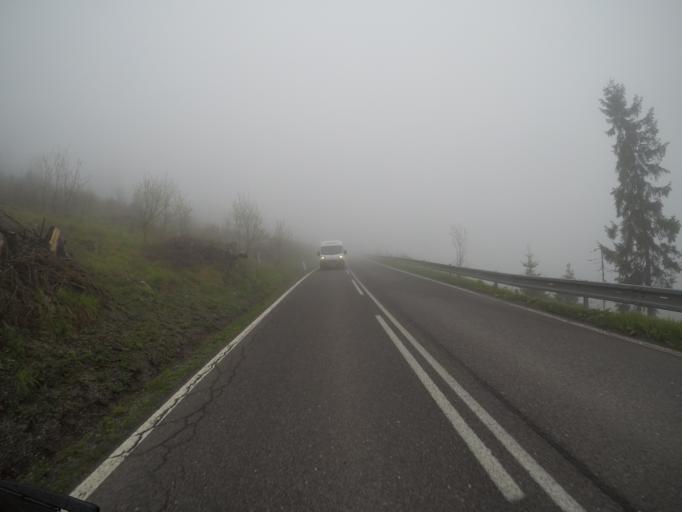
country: SK
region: Presovsky
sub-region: Okres Poprad
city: Strba
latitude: 49.1087
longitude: 20.0614
